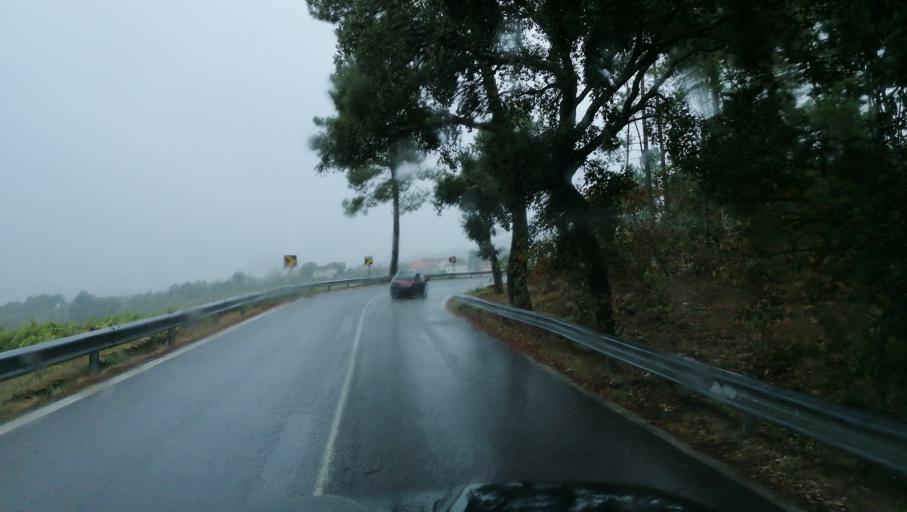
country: PT
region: Braga
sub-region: Cabeceiras de Basto
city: Cabeceiras de Basto
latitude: 41.4974
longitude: -7.9025
